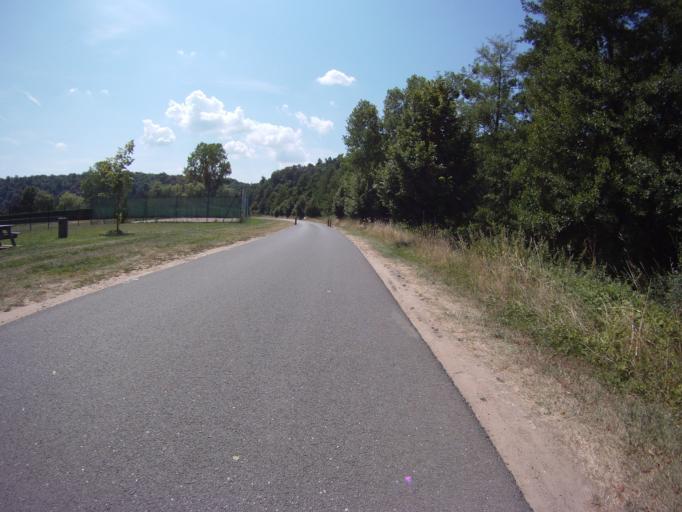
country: FR
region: Lorraine
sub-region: Departement de Meurthe-et-Moselle
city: Liverdun
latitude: 48.7498
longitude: 6.0565
